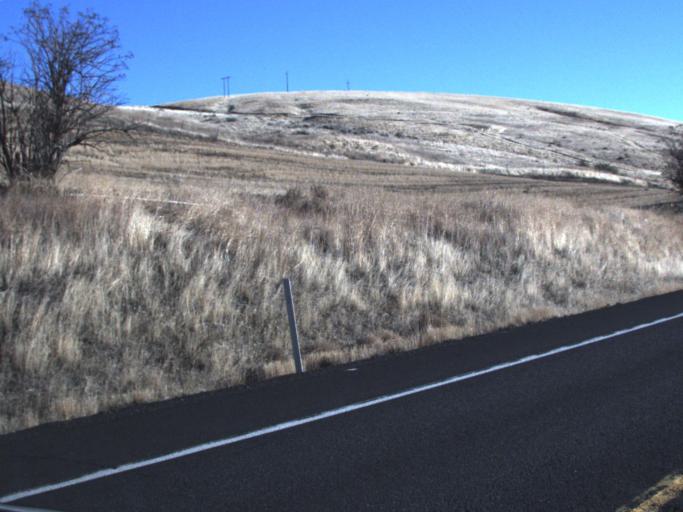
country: US
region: Washington
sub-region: Garfield County
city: Pomeroy
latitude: 46.4697
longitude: -117.5165
